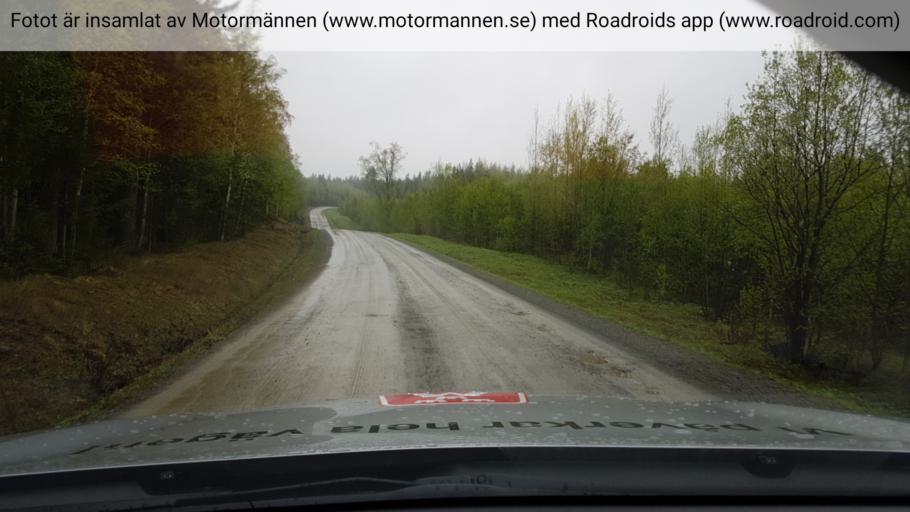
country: SE
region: Jaemtland
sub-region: Bergs Kommun
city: Hoverberg
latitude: 62.9832
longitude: 14.2020
